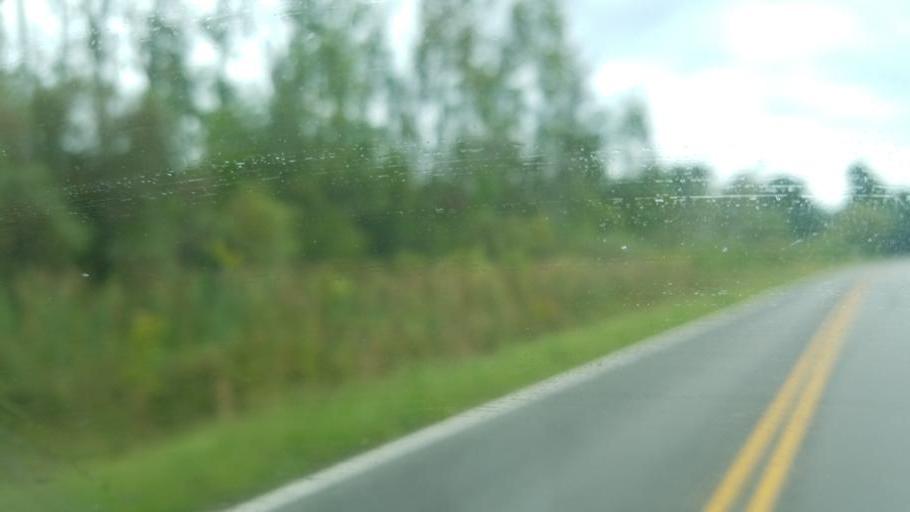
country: US
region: North Carolina
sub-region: Tyrrell County
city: Columbia
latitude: 35.9457
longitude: -76.2945
